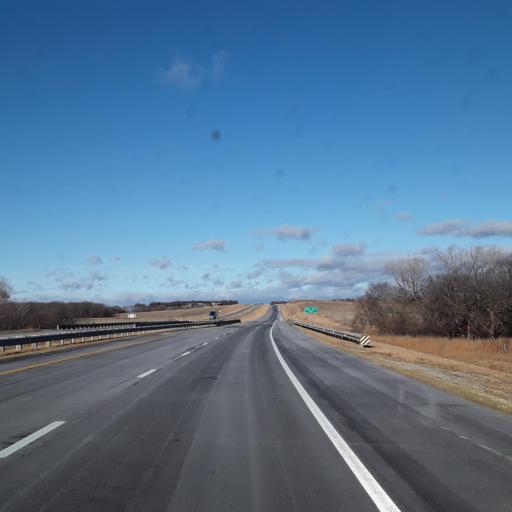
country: US
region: Kansas
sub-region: Republic County
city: Belleville
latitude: 39.7308
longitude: -97.6597
